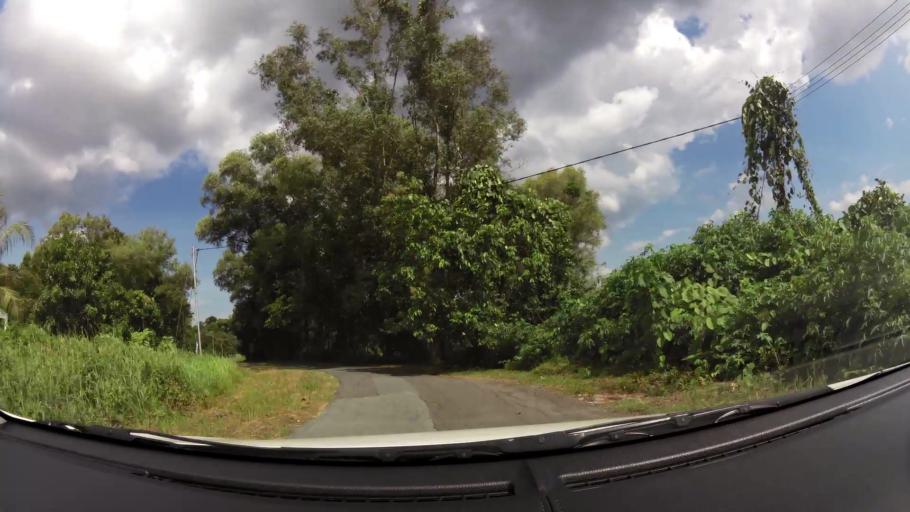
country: BN
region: Brunei and Muara
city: Bandar Seri Begawan
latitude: 4.9543
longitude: 114.9565
